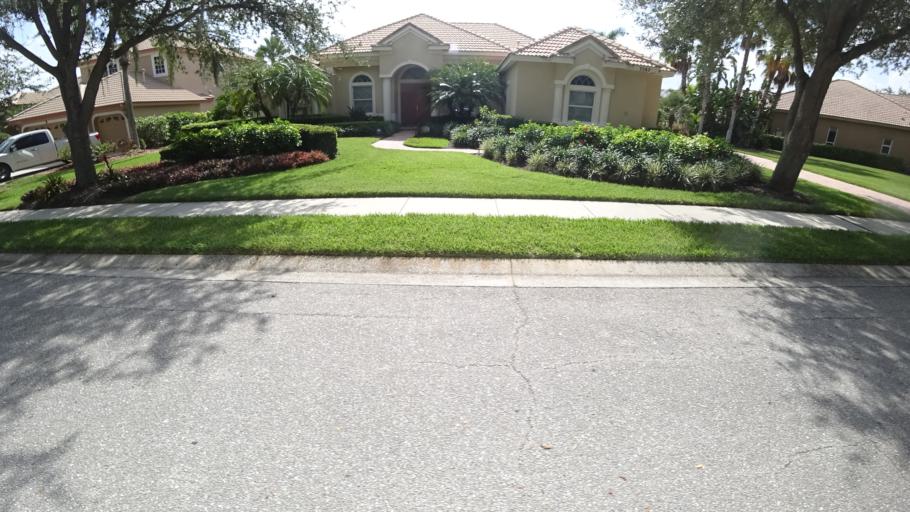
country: US
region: Florida
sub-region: Sarasota County
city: The Meadows
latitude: 27.4031
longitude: -82.4462
